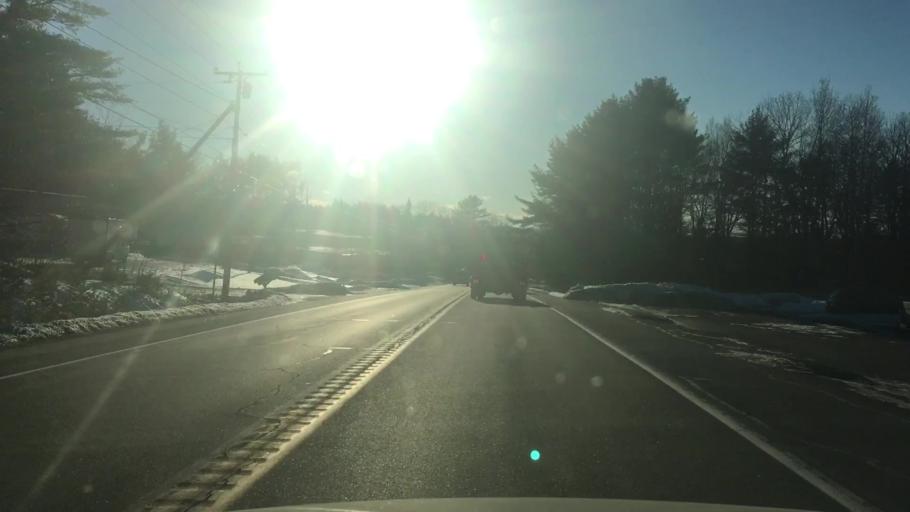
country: US
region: Maine
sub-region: Somerset County
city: Skowhegan
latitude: 44.7409
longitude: -69.7508
